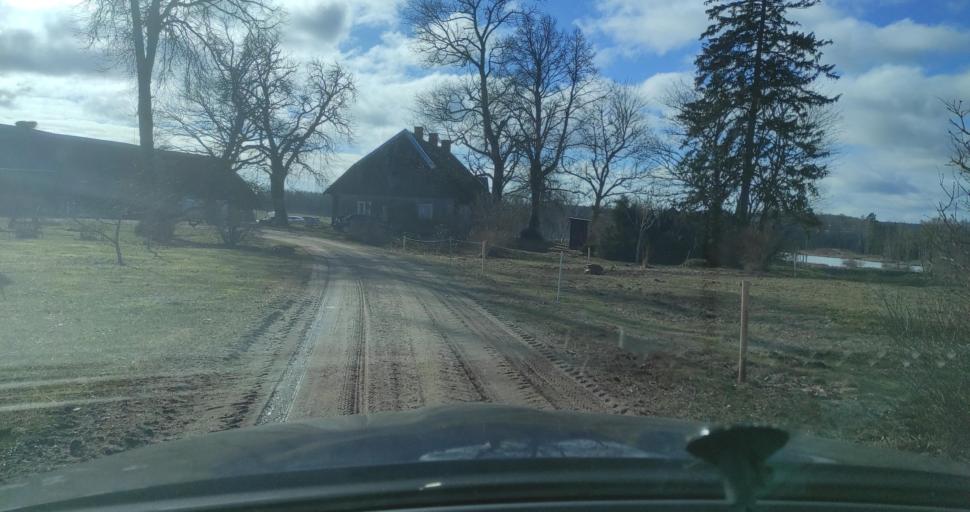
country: LV
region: Vainode
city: Vainode
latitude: 56.5138
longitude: 21.8599
